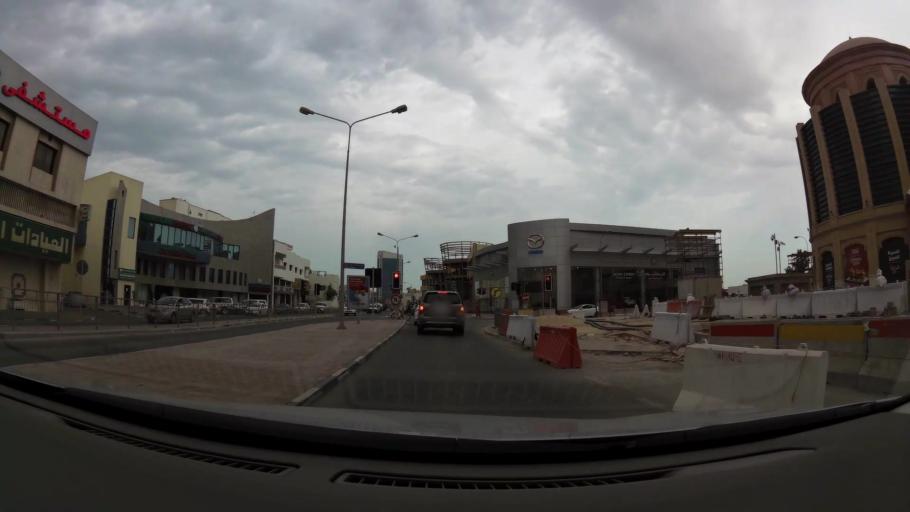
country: QA
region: Baladiyat ad Dawhah
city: Doha
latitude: 25.2737
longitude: 51.5033
